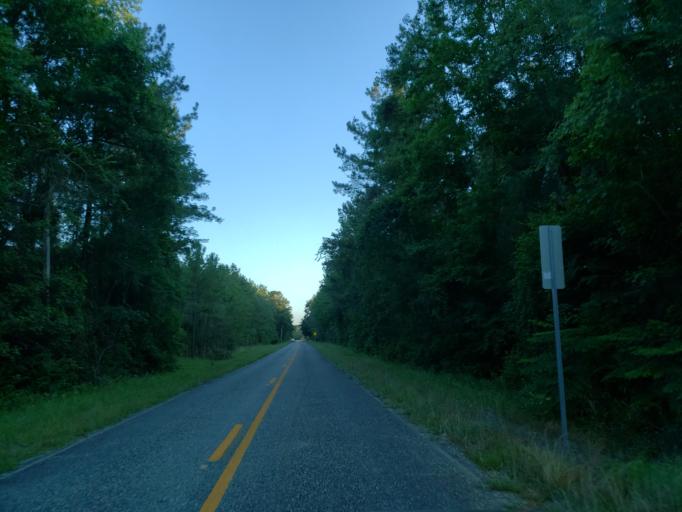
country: US
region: Georgia
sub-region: Crisp County
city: Cordele
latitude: 32.0117
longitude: -83.7544
